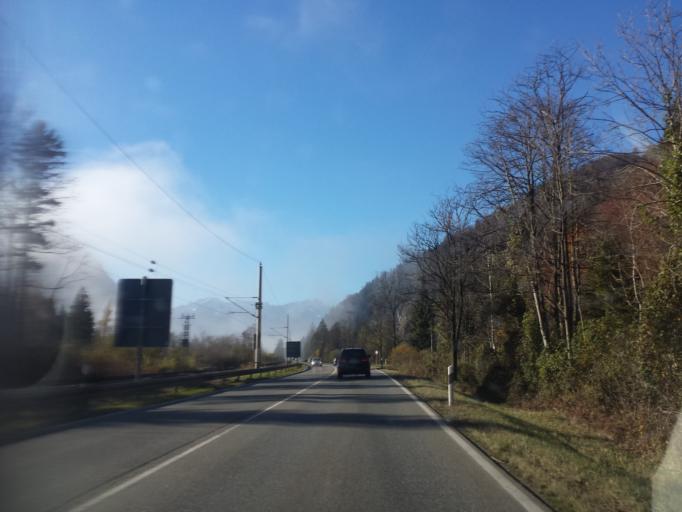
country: DE
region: Bavaria
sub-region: Upper Bavaria
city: Eschenlohe
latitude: 47.5860
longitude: 11.1733
